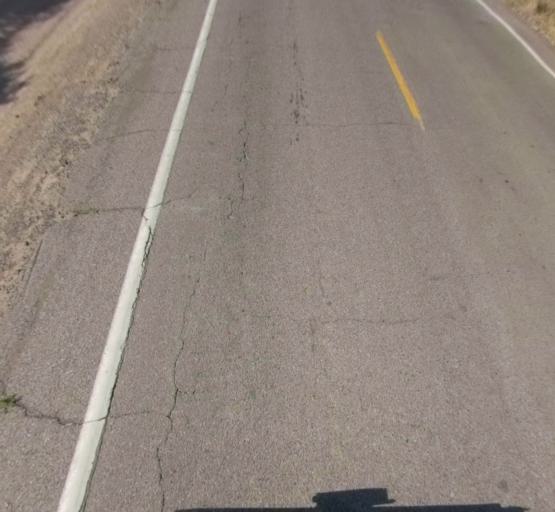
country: US
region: California
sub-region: Madera County
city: Fairmead
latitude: 36.9759
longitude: -120.2559
